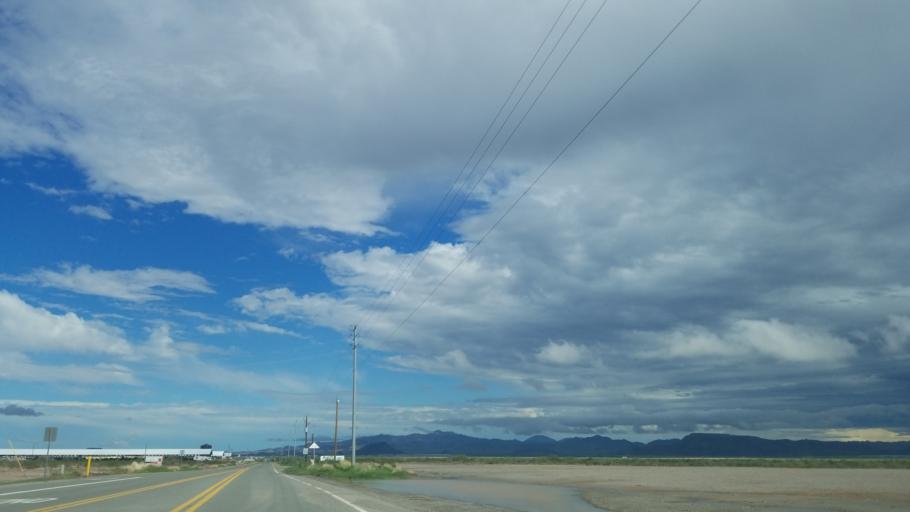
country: US
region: Arizona
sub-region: La Paz County
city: Salome
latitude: 33.6339
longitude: -113.7669
